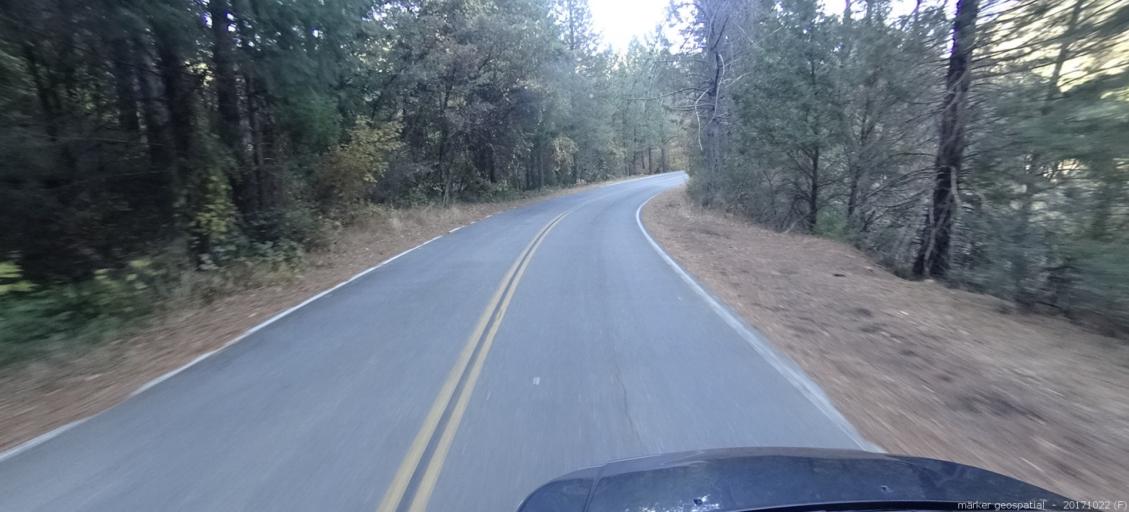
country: US
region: California
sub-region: Siskiyou County
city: Dunsmuir
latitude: 40.9324
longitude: -122.2509
